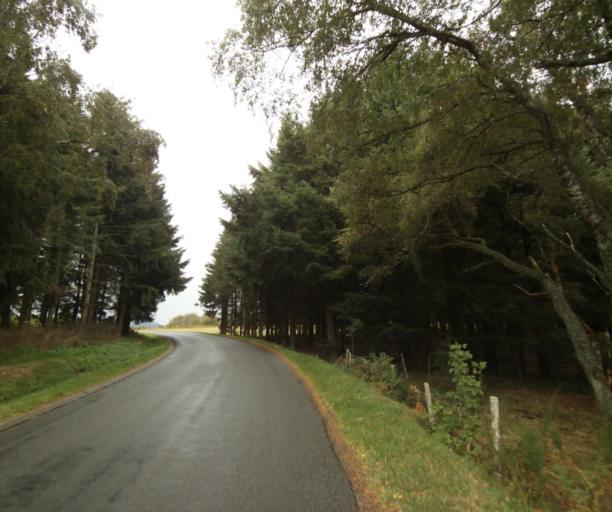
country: FR
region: Auvergne
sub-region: Departement du Puy-de-Dome
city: Saint-Genes-Champanelle
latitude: 45.7308
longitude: 2.9725
